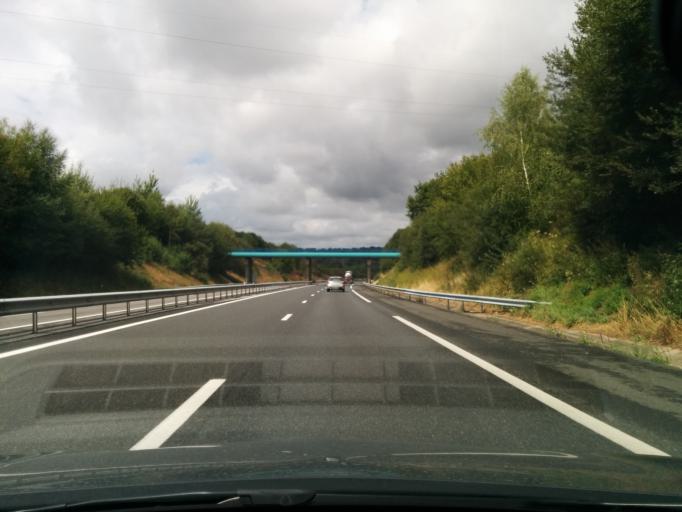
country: FR
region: Limousin
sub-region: Departement de la Correze
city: Uzerche
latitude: 45.4072
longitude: 1.5393
